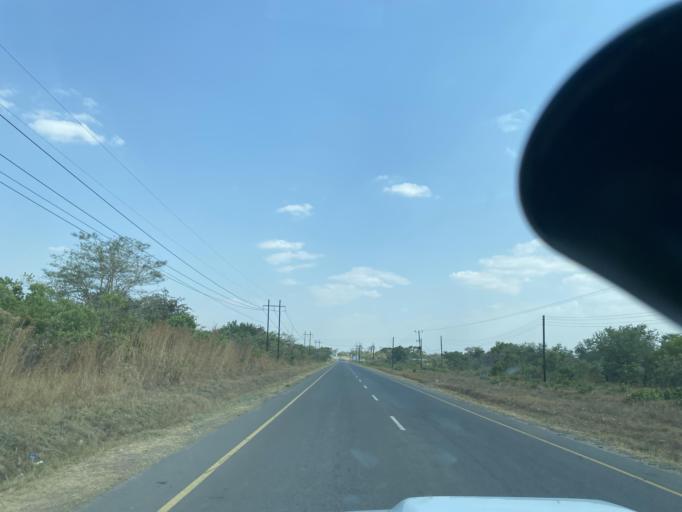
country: ZM
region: Lusaka
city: Lusaka
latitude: -15.3329
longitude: 28.0716
